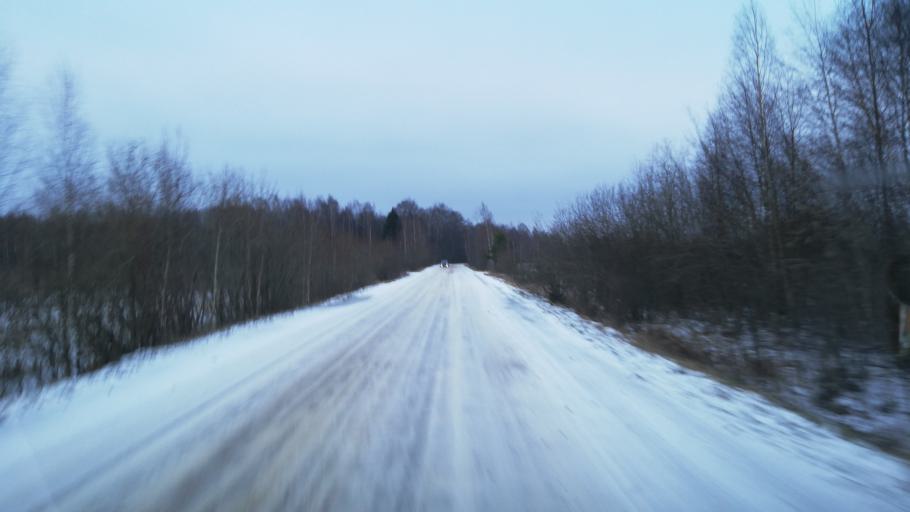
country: RU
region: Kostroma
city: Krasnoye-na-Volge
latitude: 57.6887
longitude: 41.1795
